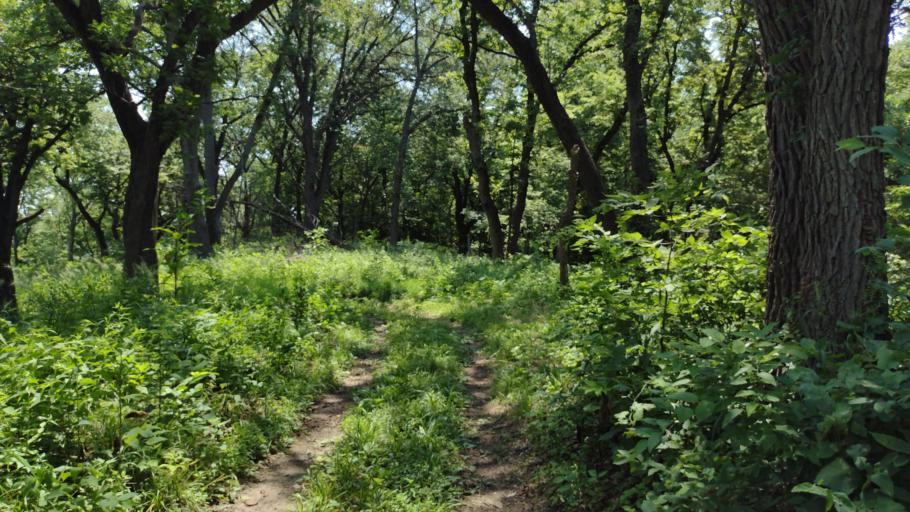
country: US
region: Nebraska
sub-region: Sarpy County
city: Bellevue
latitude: 41.1599
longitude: -95.8921
